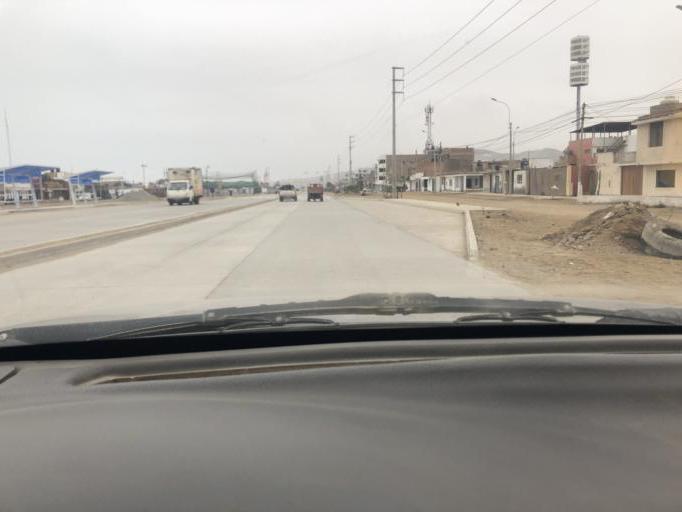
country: PE
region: Lima
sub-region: Lima
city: San Bartolo
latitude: -12.3676
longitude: -76.7924
